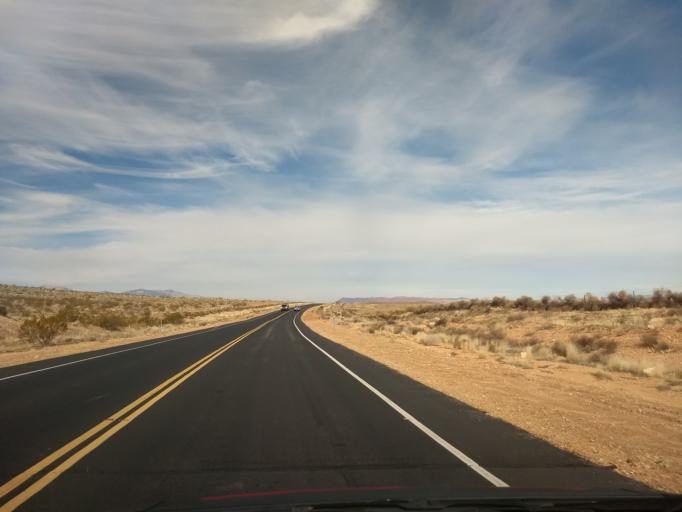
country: US
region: Utah
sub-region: Washington County
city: Washington
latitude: 37.0163
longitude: -113.4972
